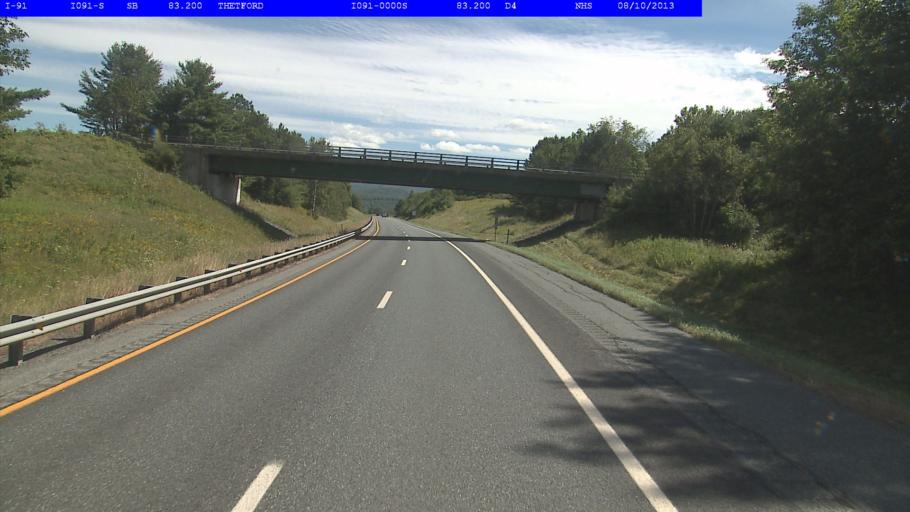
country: US
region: New Hampshire
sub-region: Grafton County
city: Lyme
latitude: 43.7984
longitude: -72.2197
